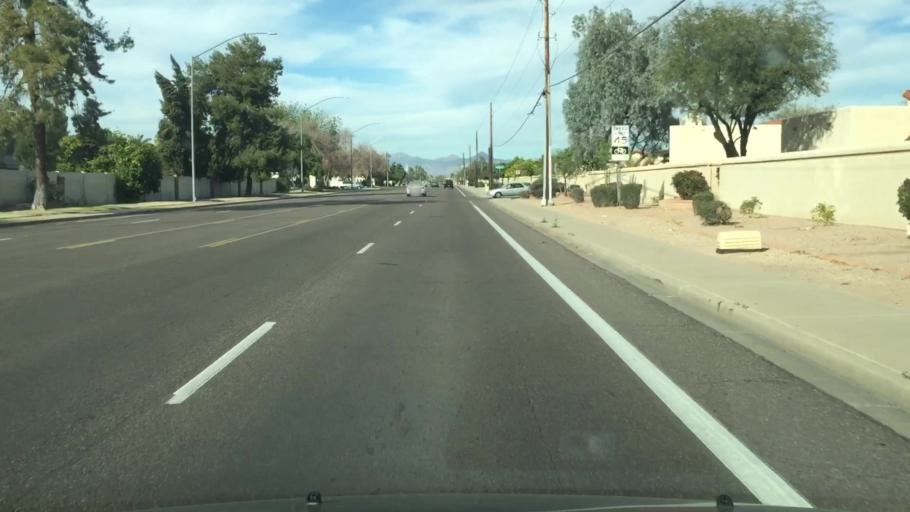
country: US
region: Arizona
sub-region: Maricopa County
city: Mesa
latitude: 33.4414
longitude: -111.8051
